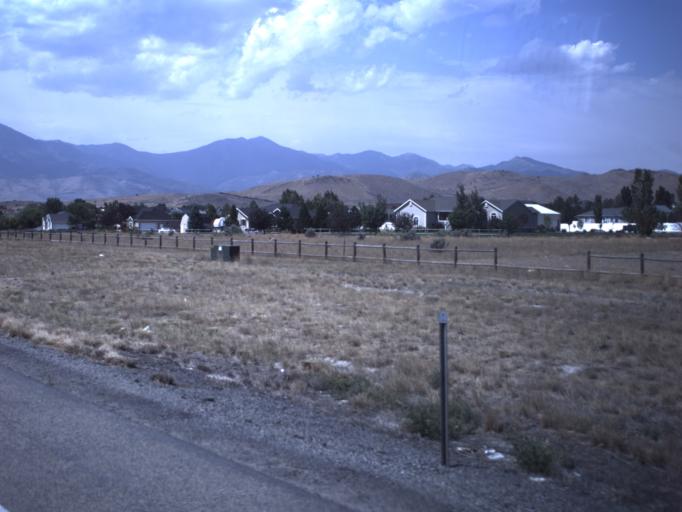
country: US
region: Utah
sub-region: Utah County
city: Eagle Mountain
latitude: 40.3794
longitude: -111.9959
